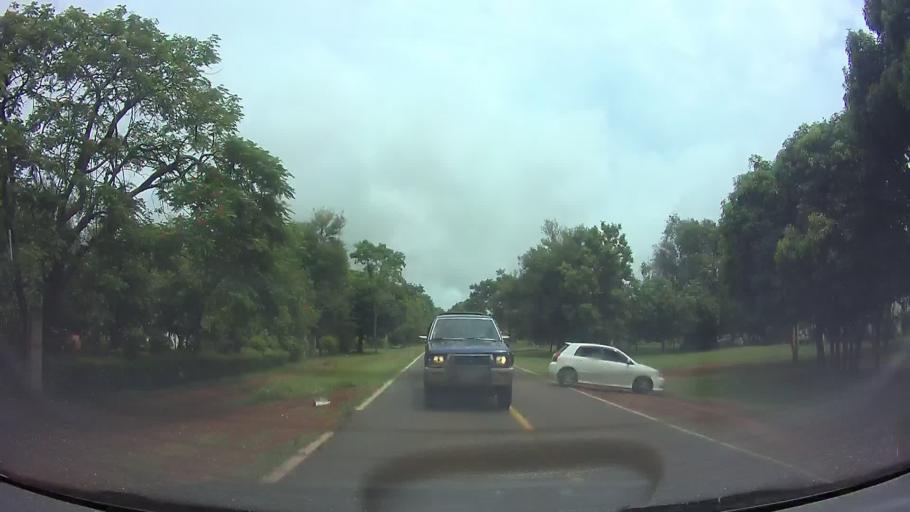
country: PY
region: Paraguari
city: Ybycui
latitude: -25.9631
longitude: -57.0860
